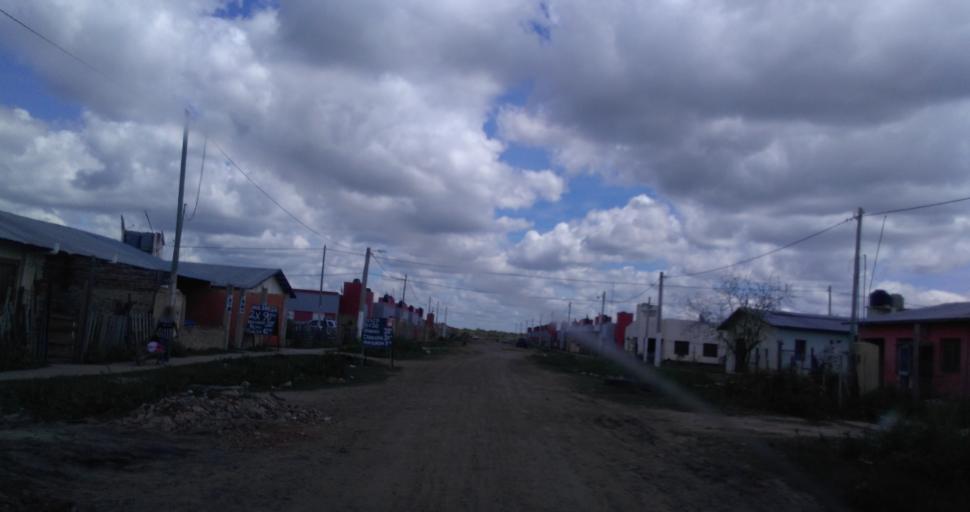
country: AR
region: Chaco
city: Resistencia
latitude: -27.4835
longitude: -59.0101
